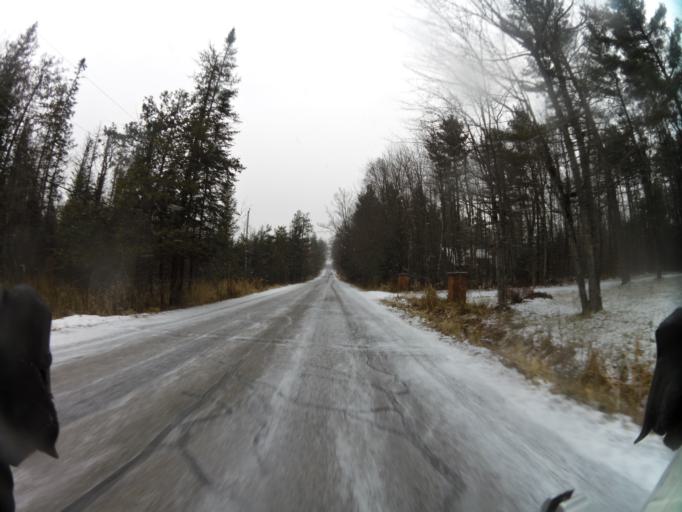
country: CA
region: Quebec
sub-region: Outaouais
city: Gatineau
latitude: 45.4888
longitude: -75.8408
